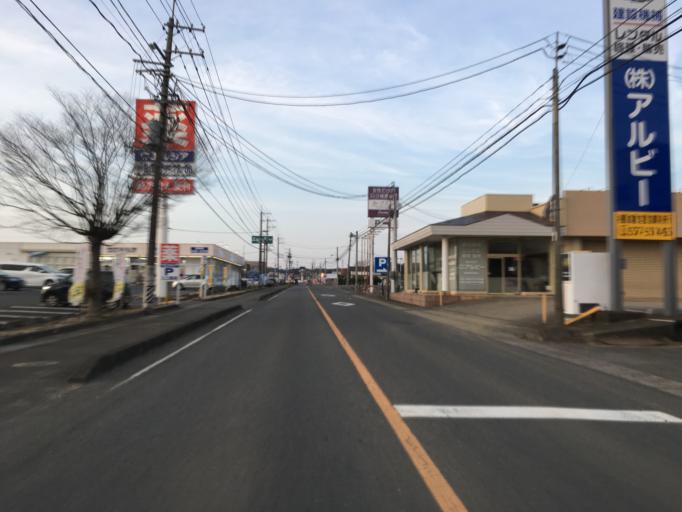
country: JP
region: Fukushima
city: Ishikawa
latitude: 37.0144
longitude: 140.3916
